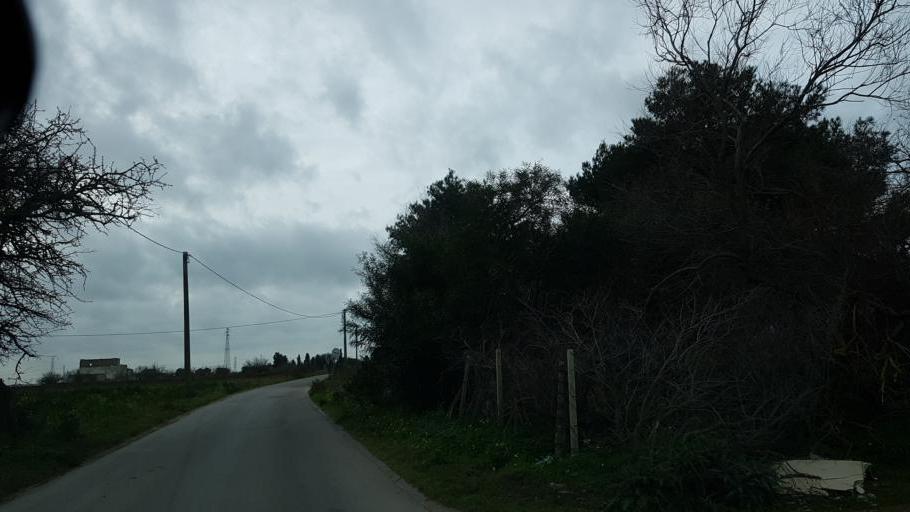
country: IT
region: Apulia
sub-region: Provincia di Brindisi
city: Brindisi
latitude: 40.6127
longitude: 17.9272
